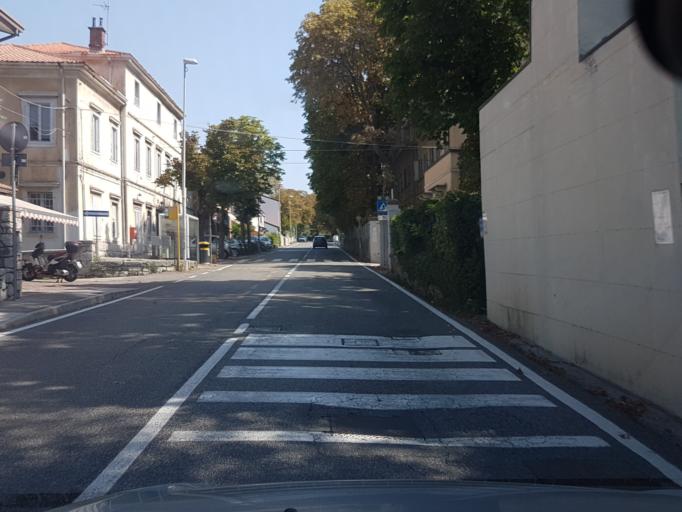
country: IT
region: Friuli Venezia Giulia
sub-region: Provincia di Trieste
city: Aurisina
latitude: 45.7511
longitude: 13.6856
